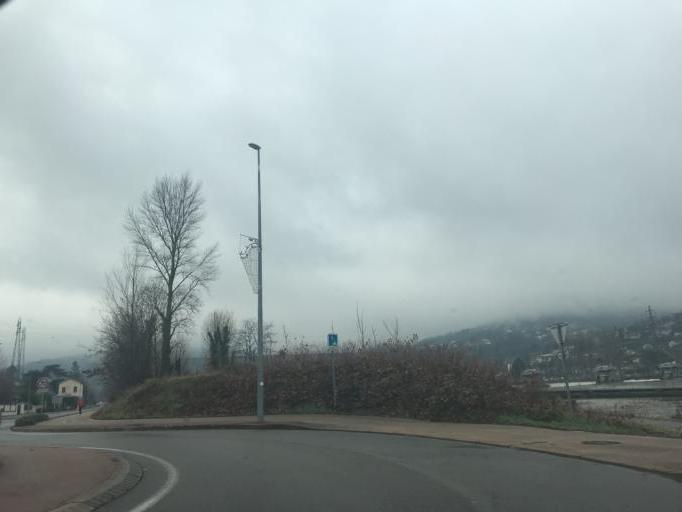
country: FR
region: Rhone-Alpes
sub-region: Departement du Rhone
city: Rochetaillee-sur-Saone
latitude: 45.8499
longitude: 4.8375
